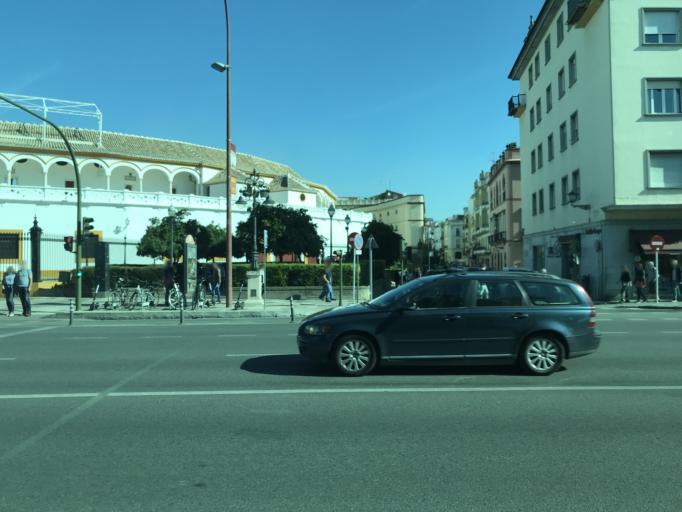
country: ES
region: Andalusia
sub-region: Provincia de Sevilla
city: Sevilla
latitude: 37.3851
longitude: -5.9988
